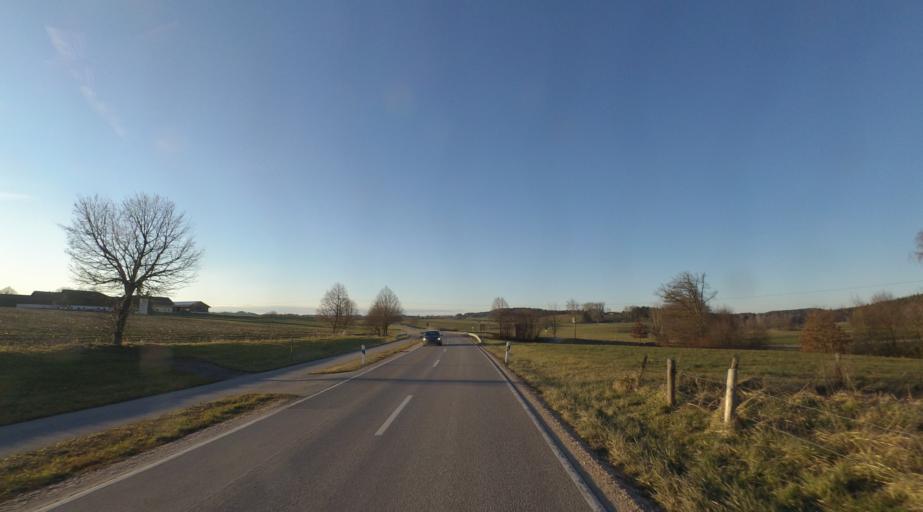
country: DE
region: Bavaria
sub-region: Upper Bavaria
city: Kirchanschoring
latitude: 47.9540
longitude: 12.7832
